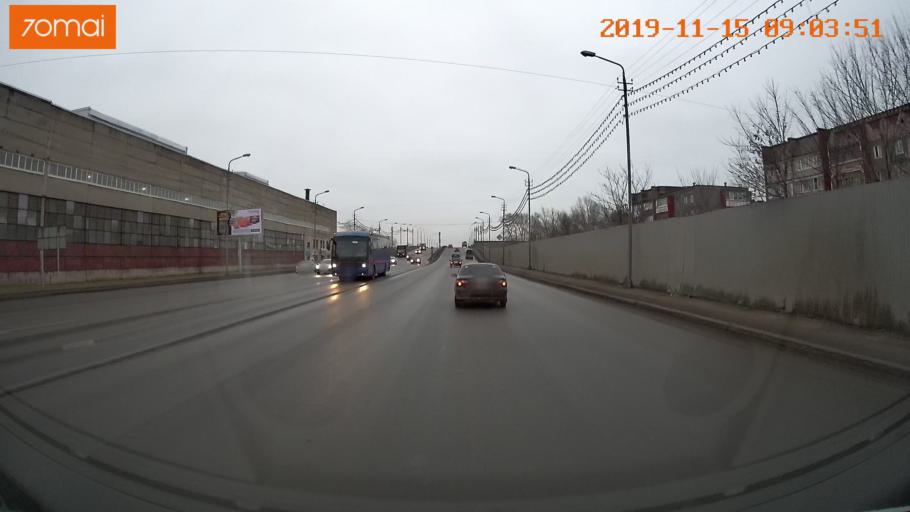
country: RU
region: Vologda
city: Cherepovets
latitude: 59.1400
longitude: 37.9194
